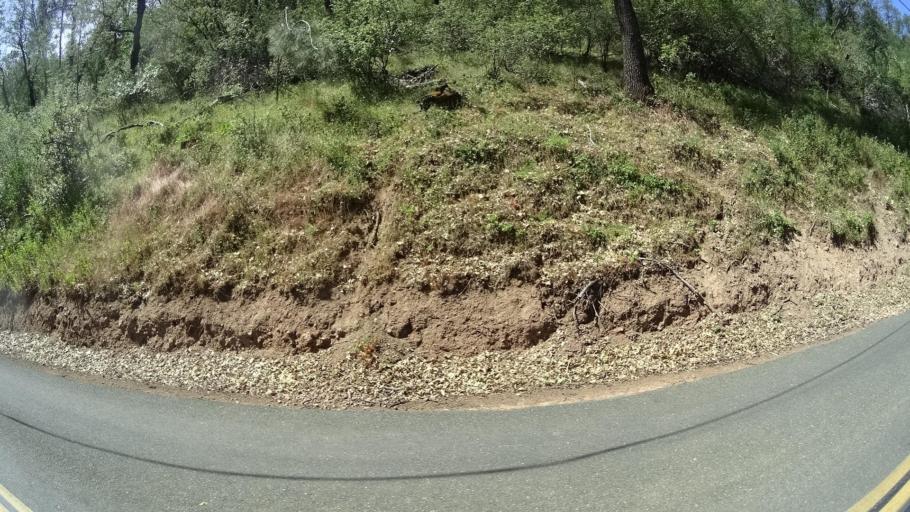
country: US
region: California
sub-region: Lake County
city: Clearlake
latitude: 38.9444
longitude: -122.6794
